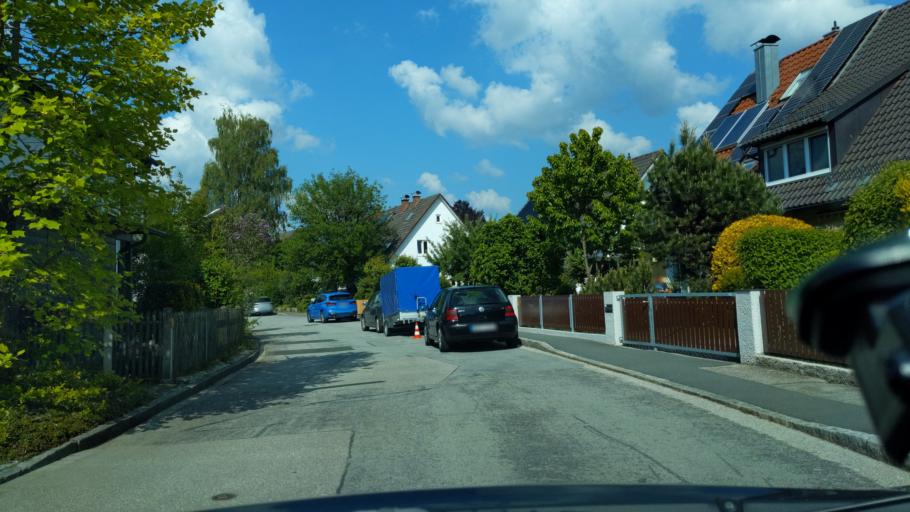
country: DE
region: Bavaria
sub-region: Upper Bavaria
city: Ebersberg
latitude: 48.0795
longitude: 11.9604
